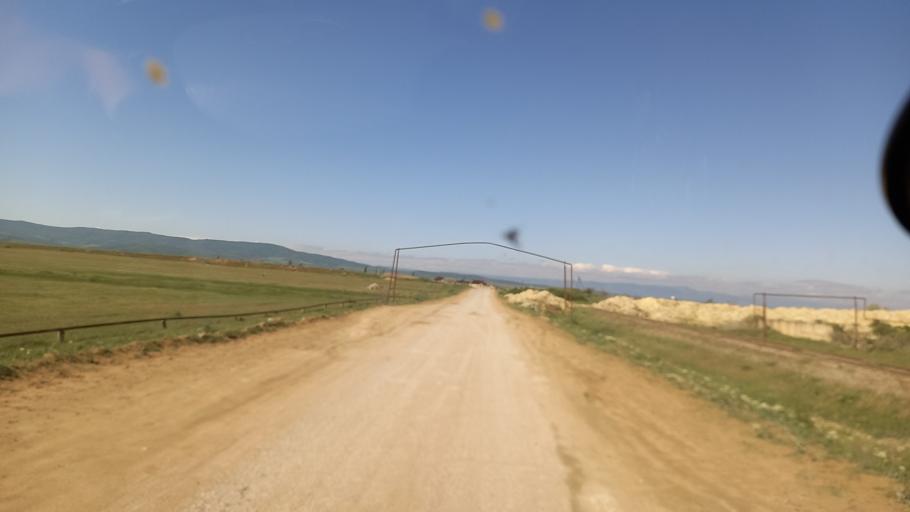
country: RU
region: Dagestan
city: Dagestanskiye Ogni
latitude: 42.1325
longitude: 48.2298
